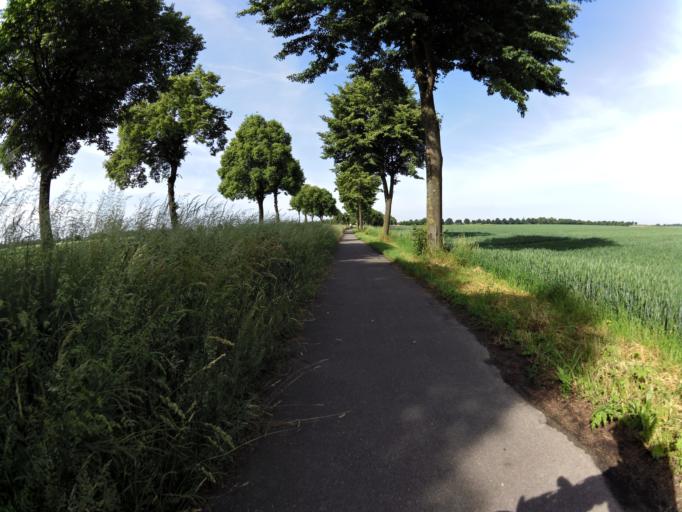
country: DE
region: North Rhine-Westphalia
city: Geilenkirchen
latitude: 50.9551
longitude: 6.0953
